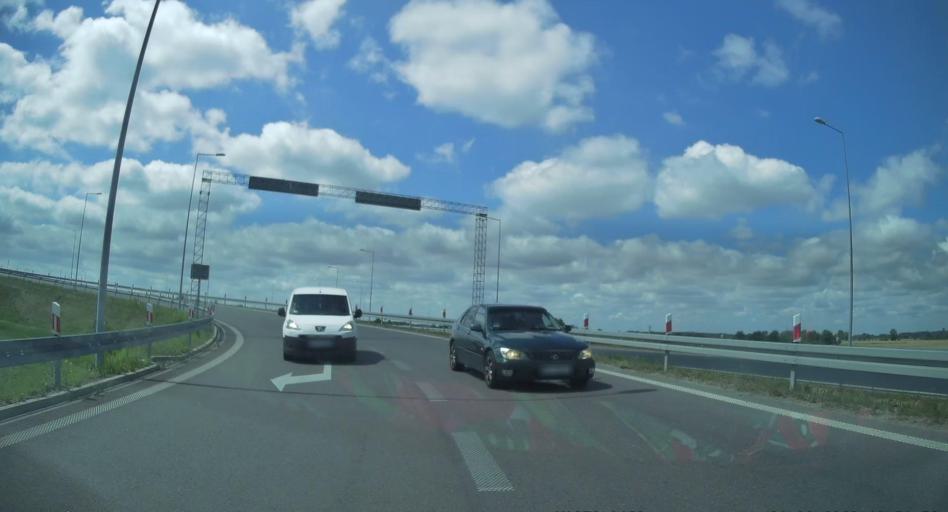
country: PL
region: Subcarpathian Voivodeship
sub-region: Powiat mielecki
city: Padew Narodowa
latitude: 50.3841
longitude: 21.4582
